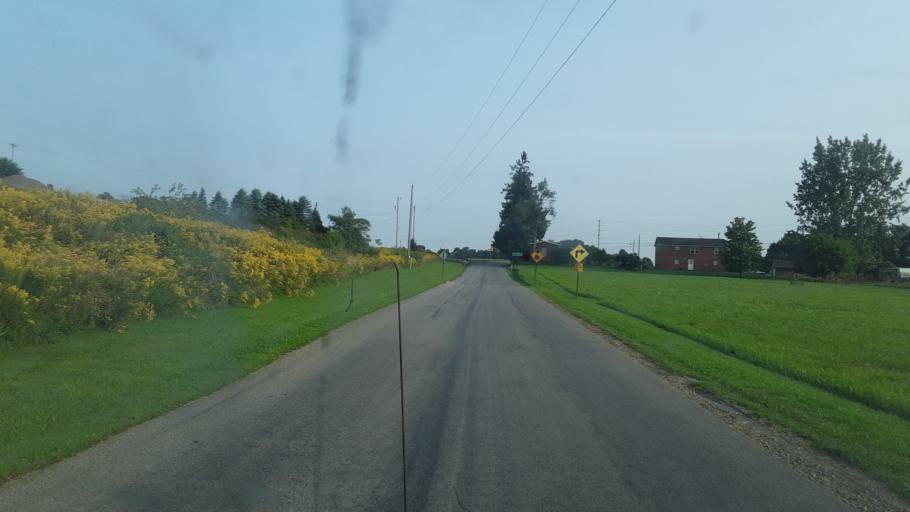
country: US
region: Pennsylvania
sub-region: Jefferson County
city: Punxsutawney
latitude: 40.9634
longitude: -79.0985
